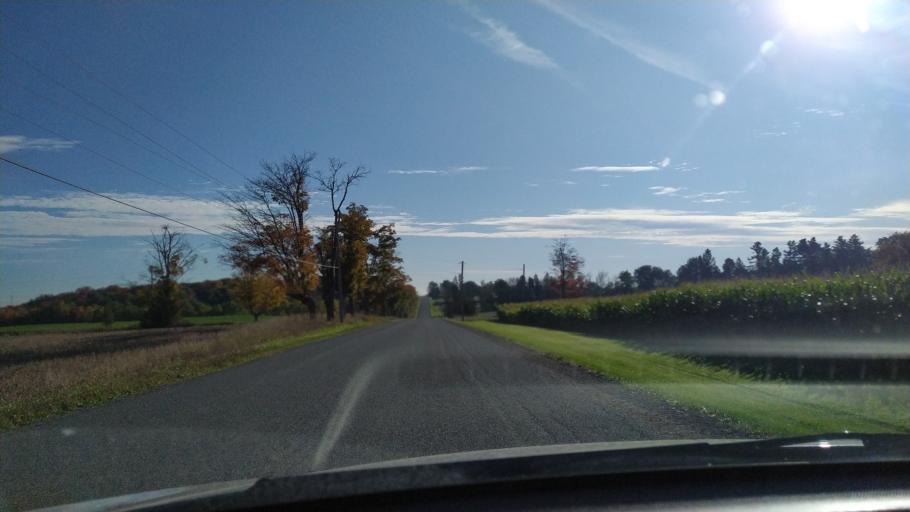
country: CA
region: Ontario
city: Stratford
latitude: 43.4618
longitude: -80.8156
